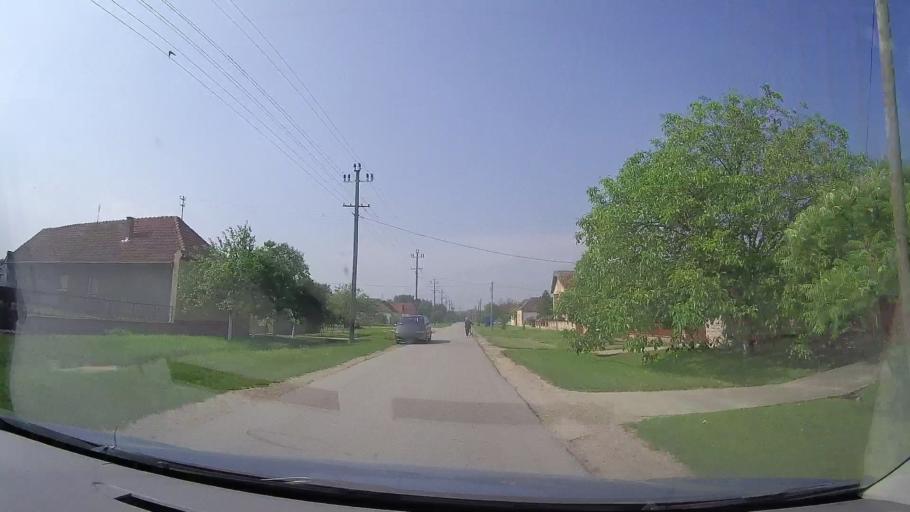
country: RS
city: Jasa Tomic
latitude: 45.4410
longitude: 20.8511
